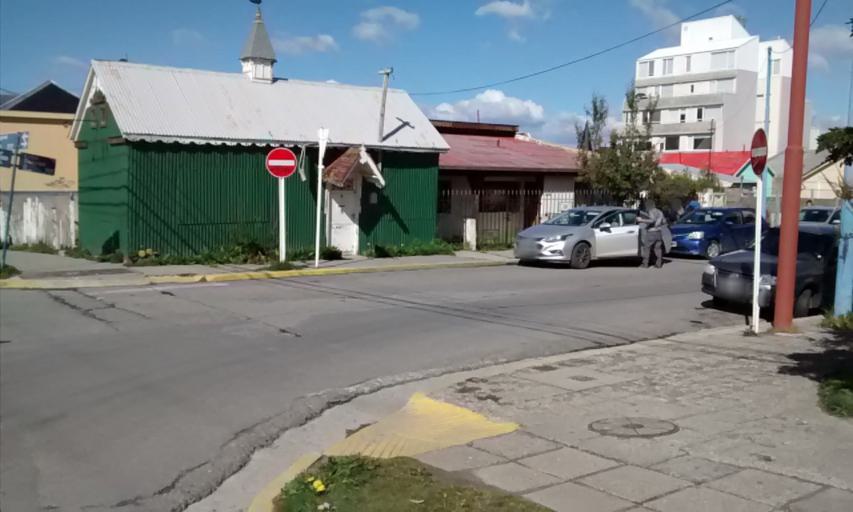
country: AR
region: Tierra del Fuego
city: Ushuaia
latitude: -54.8039
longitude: -68.2990
